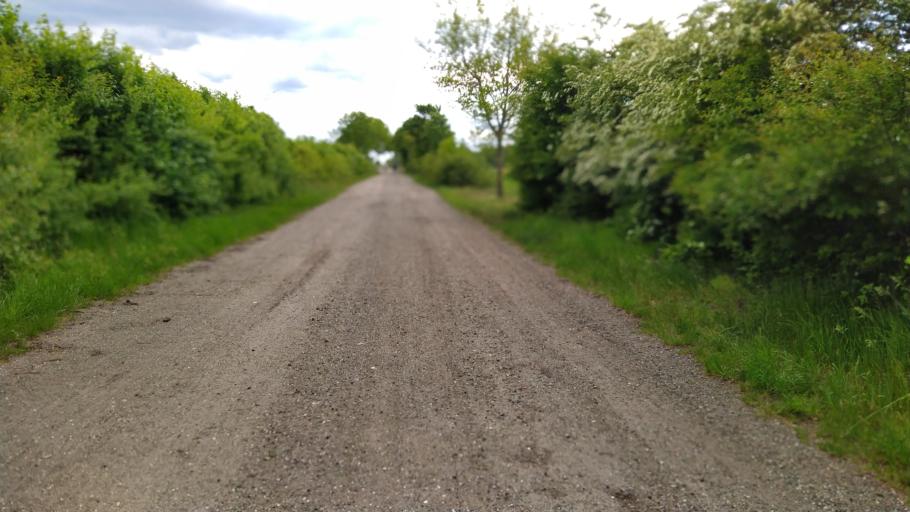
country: DE
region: Lower Saxony
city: Ahlerstedt
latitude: 53.3765
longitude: 9.3974
